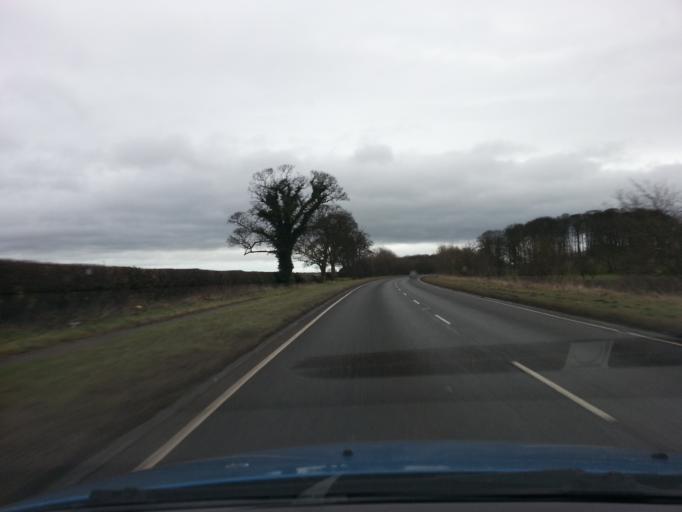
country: GB
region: England
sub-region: County Durham
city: Spennymoor
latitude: 54.6573
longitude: -1.6031
